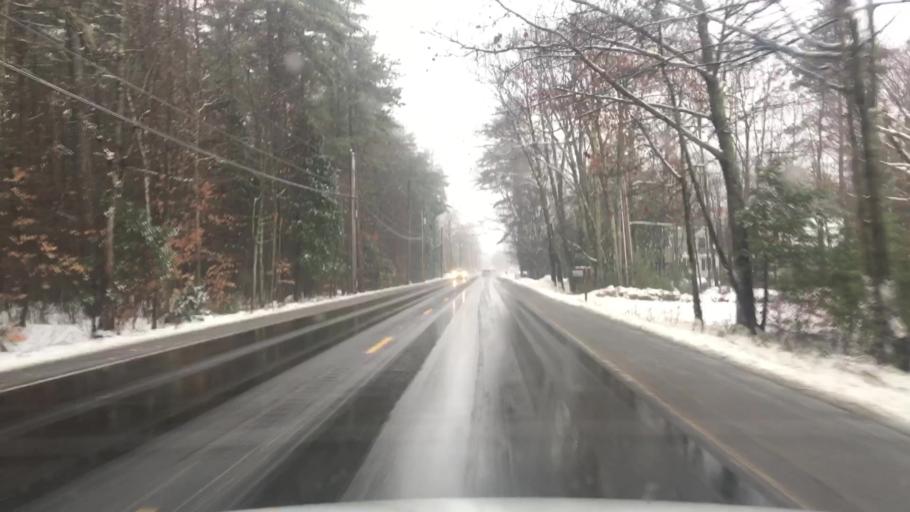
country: US
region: Maine
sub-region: York County
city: Buxton
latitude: 43.7210
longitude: -70.5274
